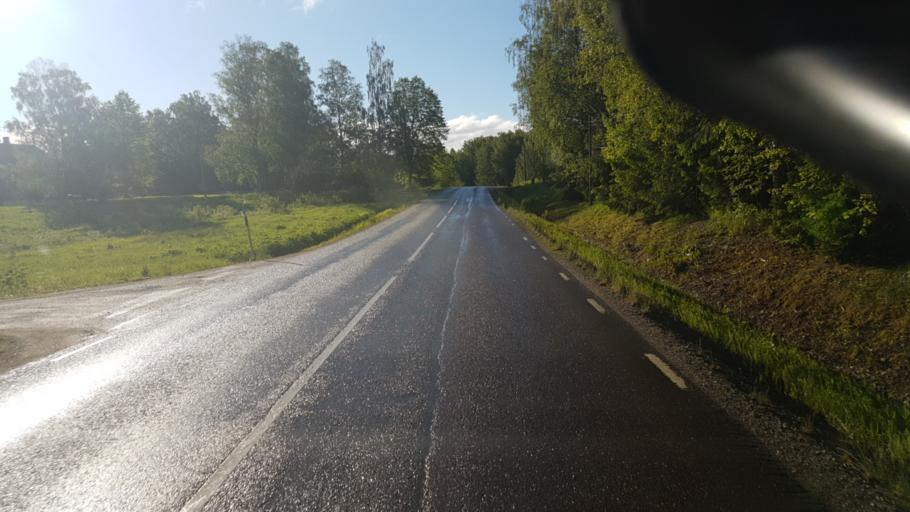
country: SE
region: Vaermland
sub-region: Arvika Kommun
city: Arvika
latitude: 59.6538
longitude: 12.4520
